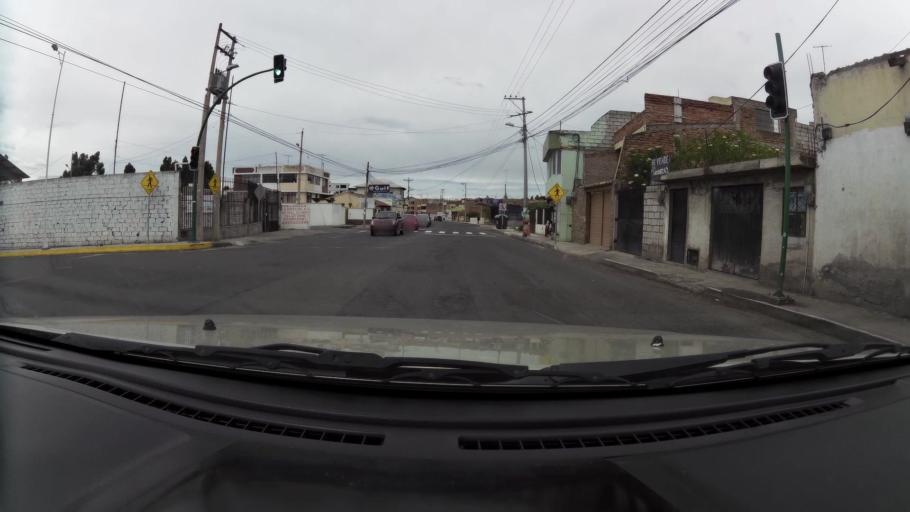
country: EC
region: Cotopaxi
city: Latacunga
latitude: -0.9481
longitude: -78.6115
